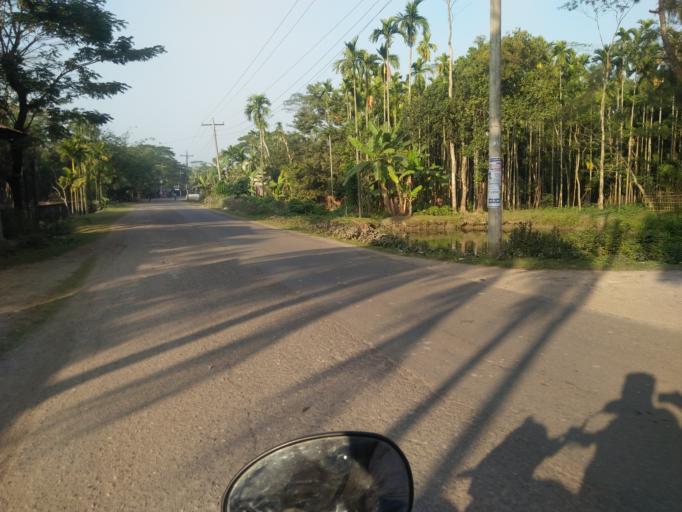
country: BD
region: Barisal
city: Bhola
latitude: 22.7482
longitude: 90.6345
